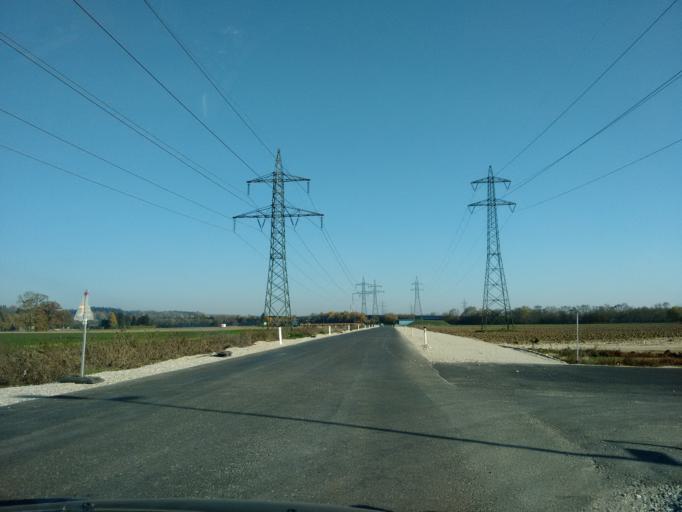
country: AT
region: Upper Austria
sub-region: Wels Stadt
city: Wels
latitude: 48.1706
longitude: 13.9866
